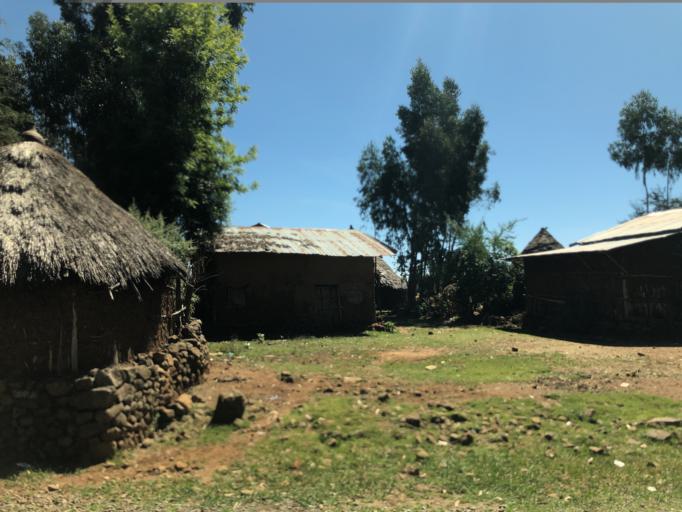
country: ET
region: Amhara
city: Lalibela
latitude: 11.6652
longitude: 38.8510
